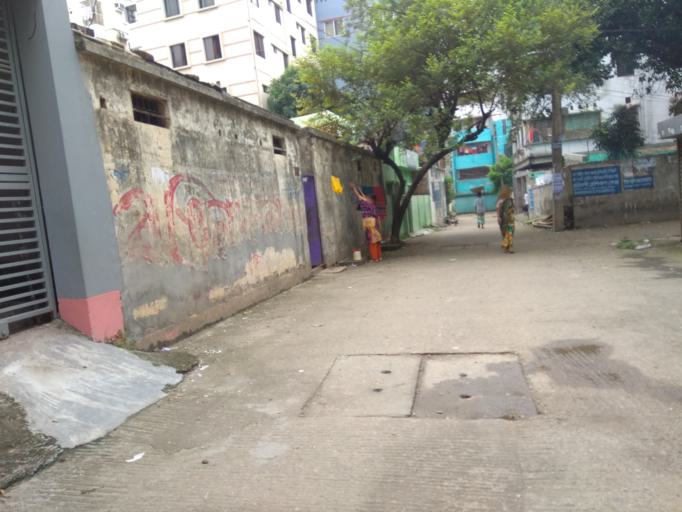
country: BD
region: Dhaka
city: Azimpur
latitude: 23.8052
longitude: 90.3581
